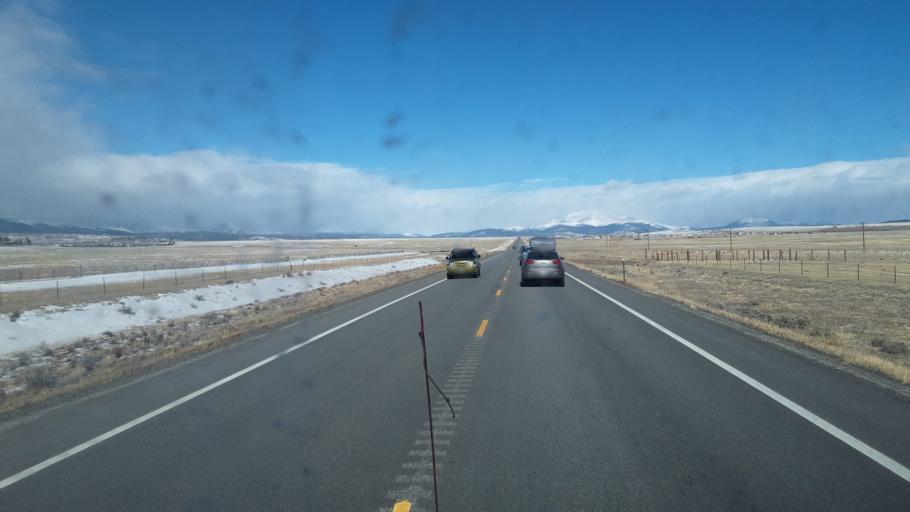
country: US
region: Colorado
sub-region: Park County
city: Fairplay
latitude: 39.1021
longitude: -105.9897
